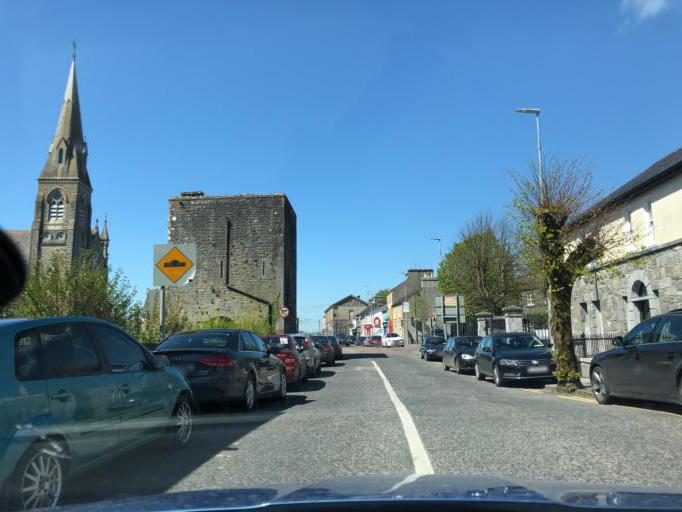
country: IE
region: Connaught
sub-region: County Galway
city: Loughrea
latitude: 53.1973
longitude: -8.5653
